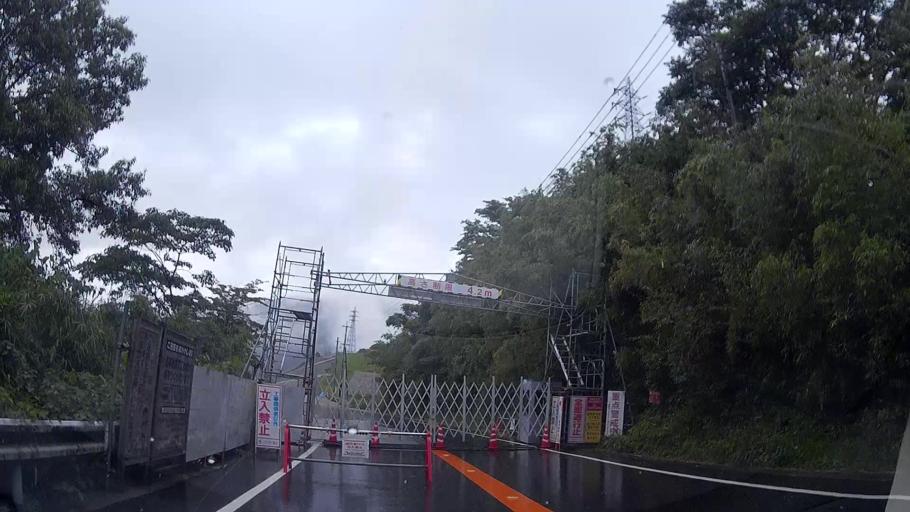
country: JP
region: Kumamoto
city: Aso
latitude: 32.8747
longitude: 130.9918
